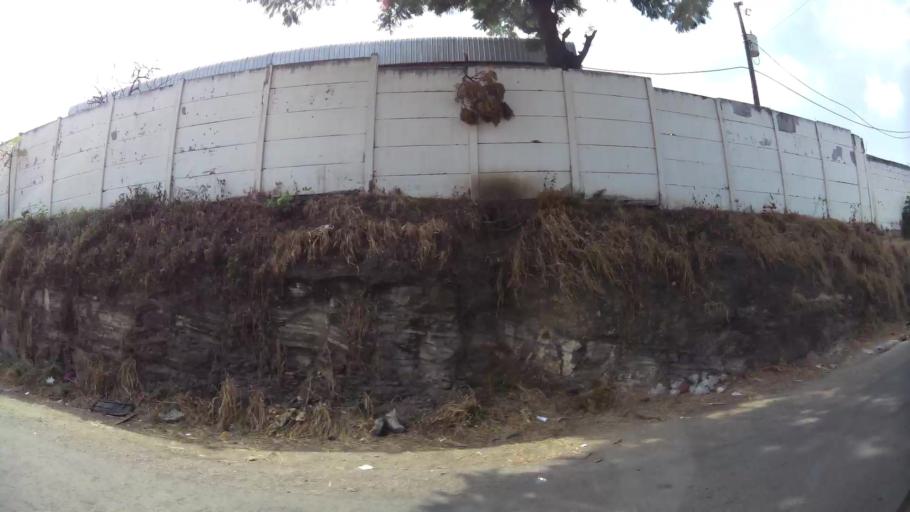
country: EC
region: Guayas
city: Guayaquil
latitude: -2.1367
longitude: -79.9393
